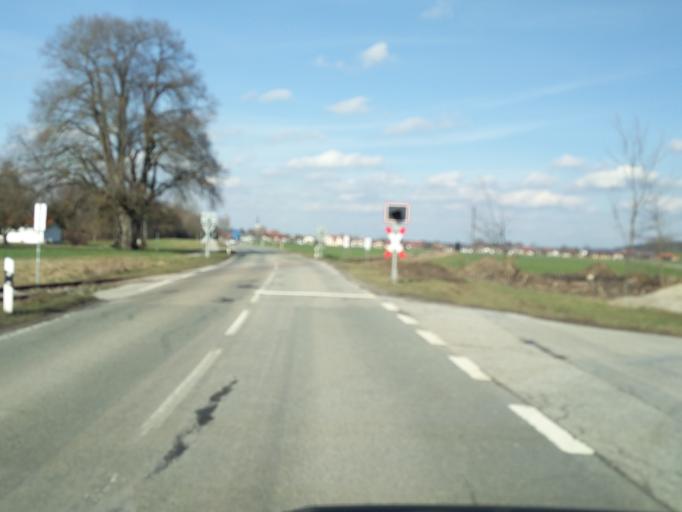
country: DE
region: Bavaria
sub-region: Upper Bavaria
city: Halfing
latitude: 47.9403
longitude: 12.2806
